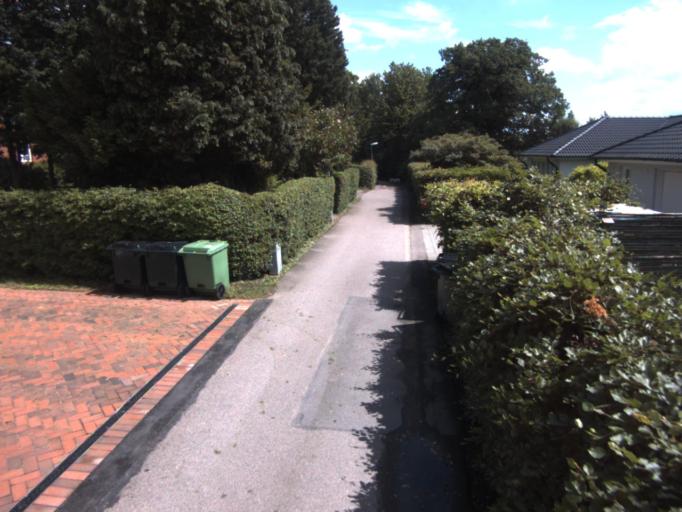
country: SE
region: Skane
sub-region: Helsingborg
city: Rydeback
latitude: 56.0225
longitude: 12.7542
